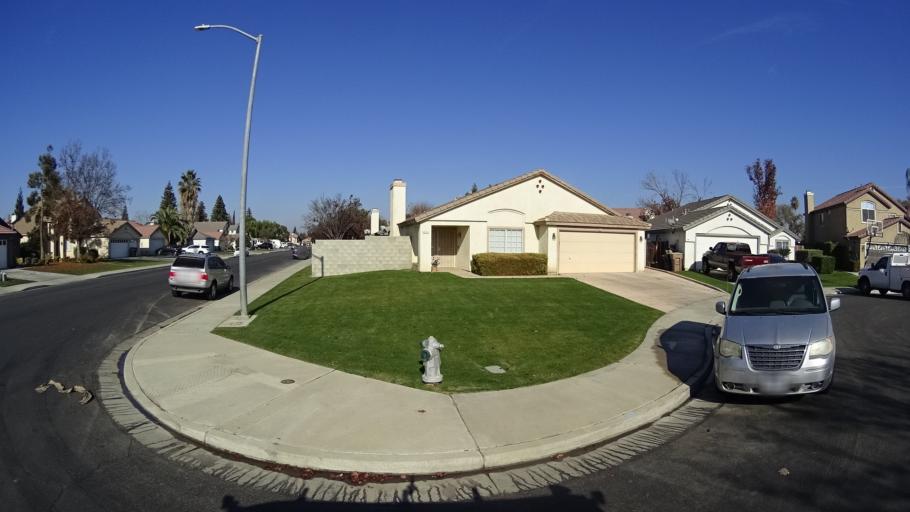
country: US
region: California
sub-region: Kern County
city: Greenacres
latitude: 35.3214
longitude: -119.1105
